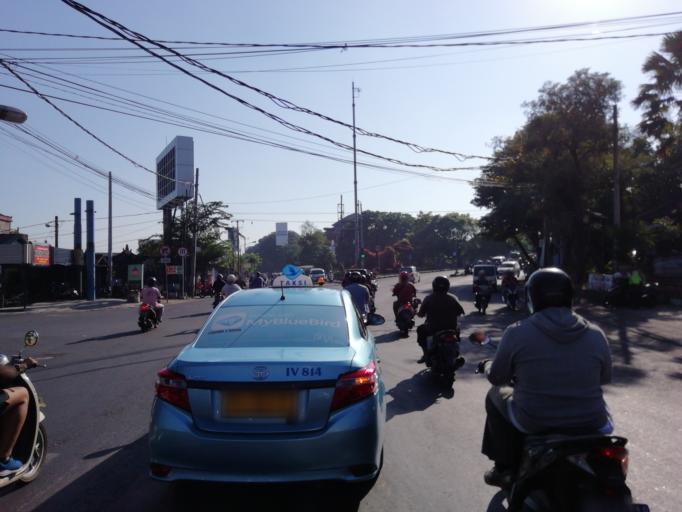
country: ID
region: Bali
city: Karyadharma
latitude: -8.6820
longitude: 115.1969
